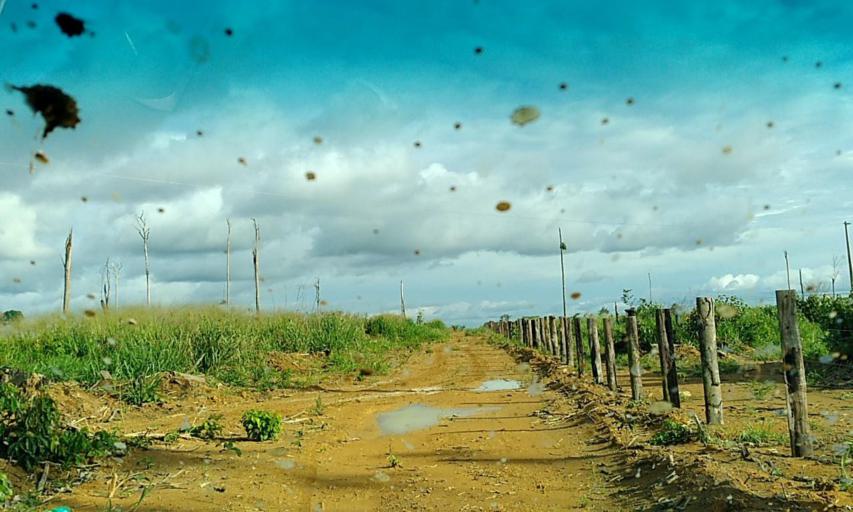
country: BR
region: Para
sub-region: Senador Jose Porfirio
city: Senador Jose Porfirio
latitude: -2.9980
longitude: -51.7421
